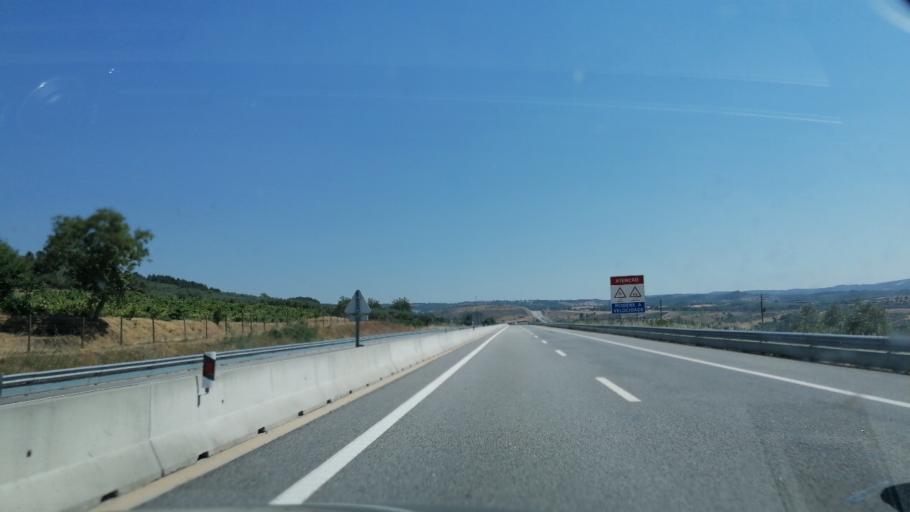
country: PT
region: Braganca
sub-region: Macedo de Cavaleiros
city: Macedo de Cavaleiros
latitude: 41.6170
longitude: -6.8731
